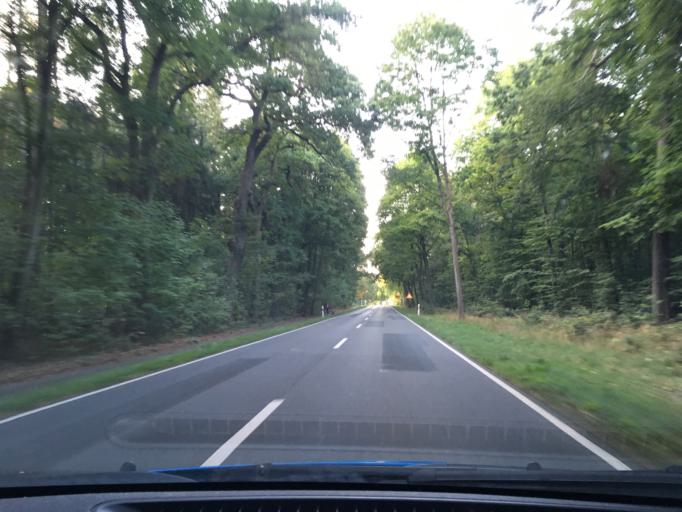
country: DE
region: Lower Saxony
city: Bleckede
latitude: 53.2773
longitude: 10.7418
